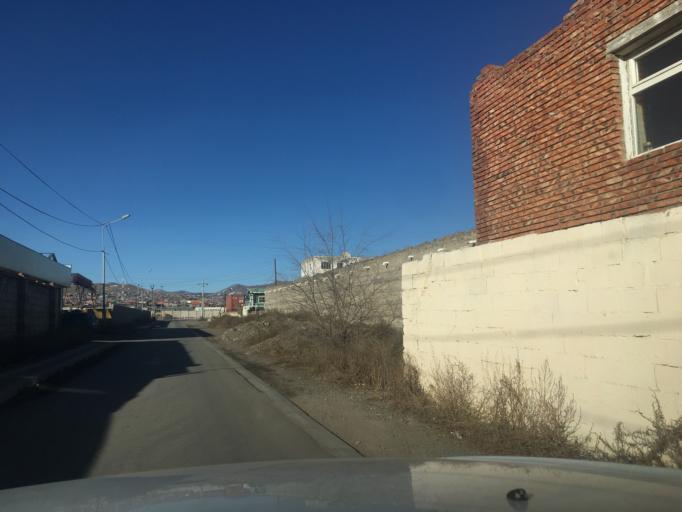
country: MN
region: Ulaanbaatar
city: Ulaanbaatar
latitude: 47.9041
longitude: 106.7648
